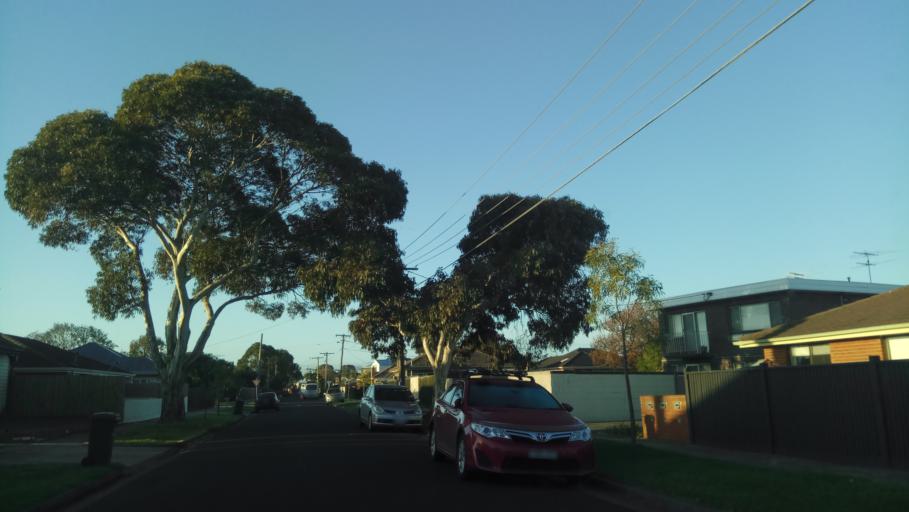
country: AU
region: Victoria
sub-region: Hobsons Bay
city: Altona
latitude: -37.8670
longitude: 144.8151
